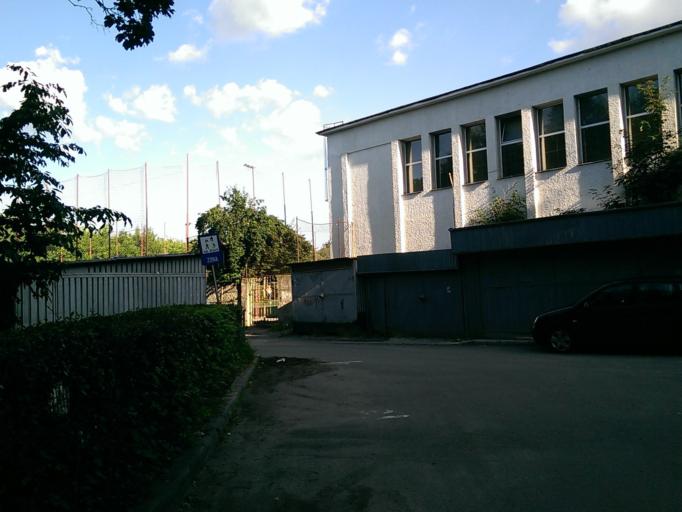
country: RO
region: Cluj
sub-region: Municipiul Cluj-Napoca
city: Cluj-Napoca
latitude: 46.7613
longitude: 23.6155
